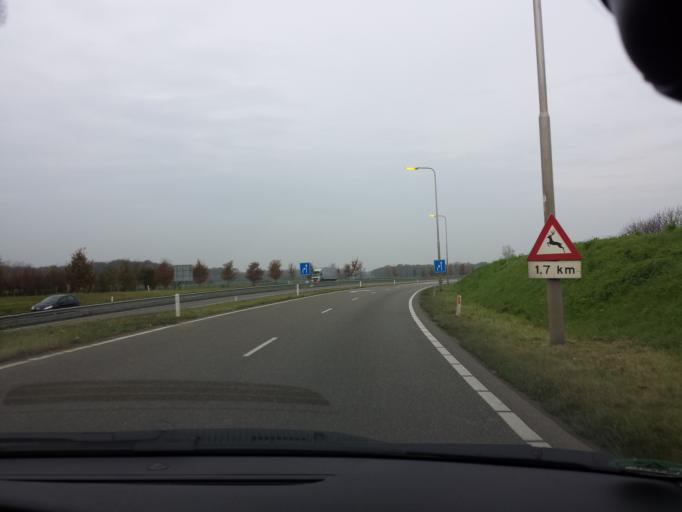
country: NL
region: Limburg
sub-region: Gemeente Sittard-Geleen
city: Limbricht
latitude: 51.0293
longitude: 5.8515
